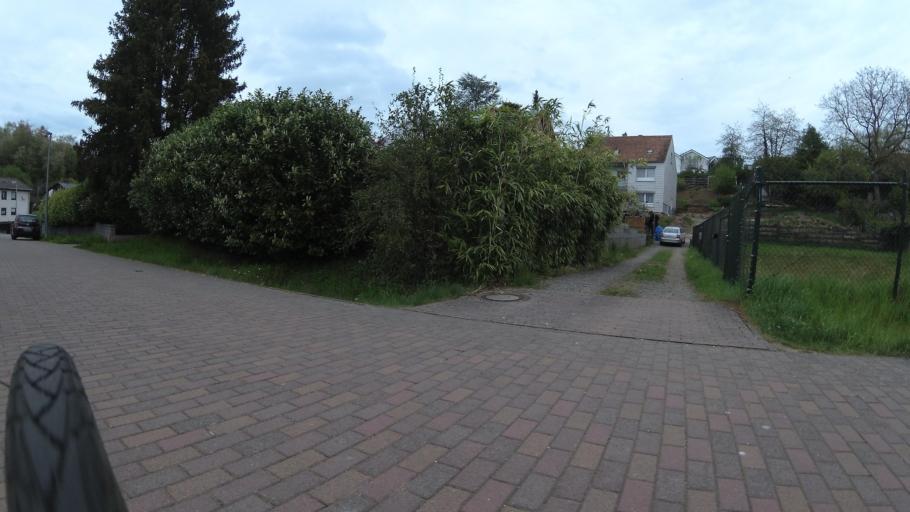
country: DE
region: Rheinland-Pfalz
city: Zweibrucken
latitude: 49.2404
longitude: 7.3537
